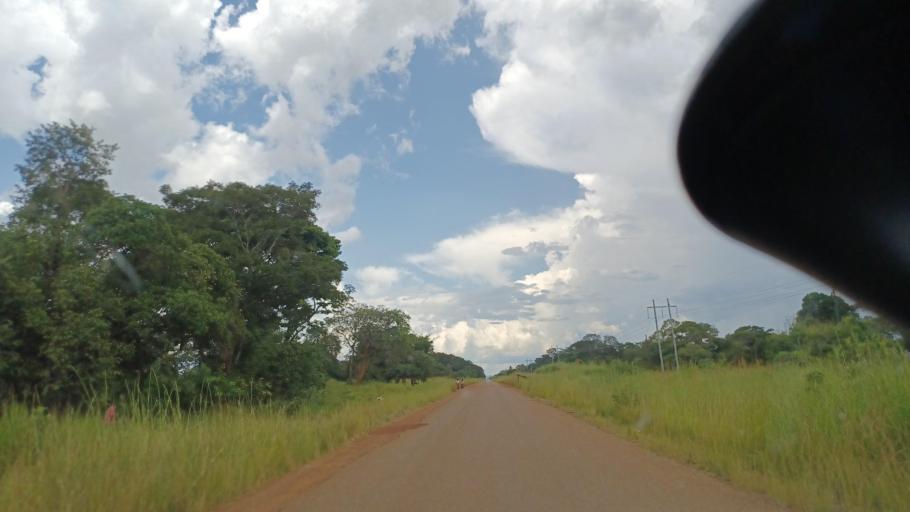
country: ZM
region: North-Western
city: Kasempa
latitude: -12.7959
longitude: 26.0165
